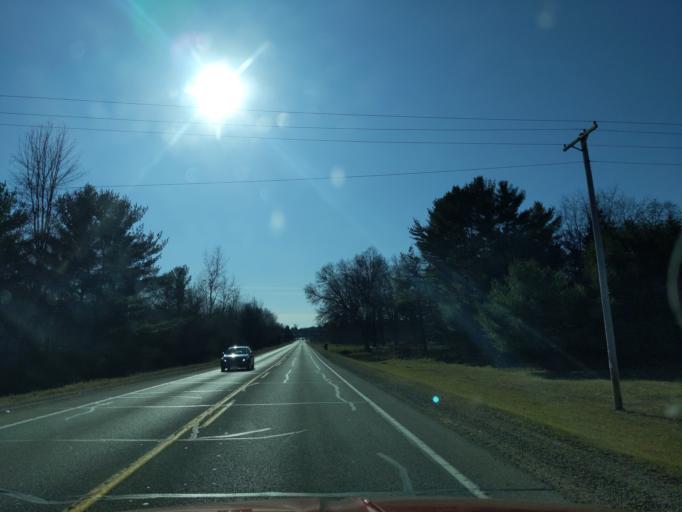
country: US
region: Wisconsin
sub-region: Waushara County
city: Wautoma
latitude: 44.0818
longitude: -89.2906
